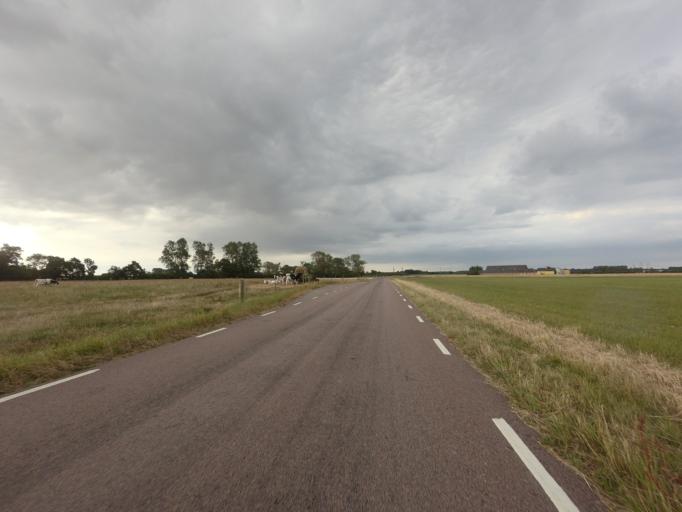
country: SE
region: Skane
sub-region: Helsingborg
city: Odakra
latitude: 56.1459
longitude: 12.7324
